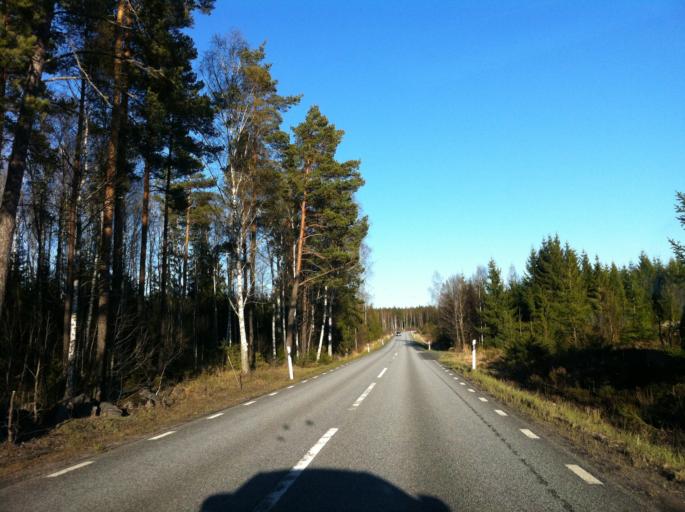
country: SE
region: Uppsala
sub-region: Osthammars Kommun
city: Anneberg
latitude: 60.1674
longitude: 18.4123
